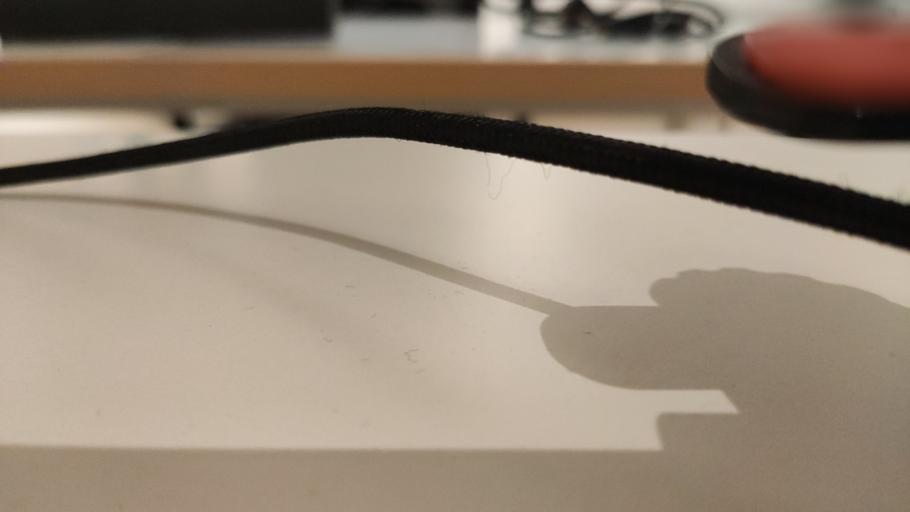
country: RU
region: Kaluga
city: Belousovo
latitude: 55.1434
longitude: 36.7688
